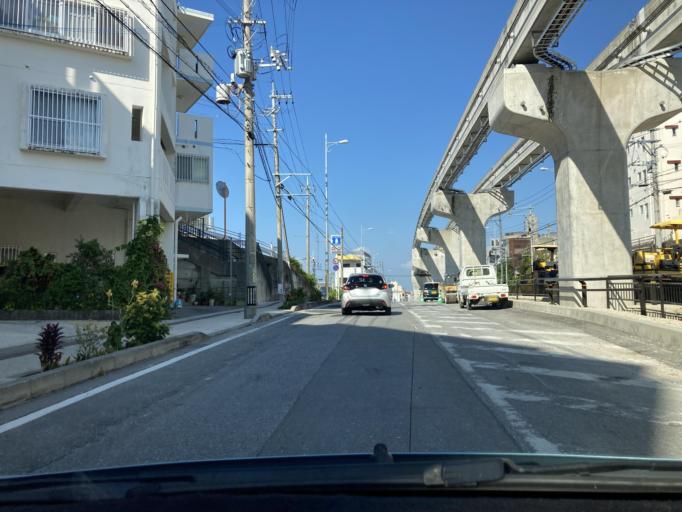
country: JP
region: Okinawa
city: Naha-shi
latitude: 26.2206
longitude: 127.7267
